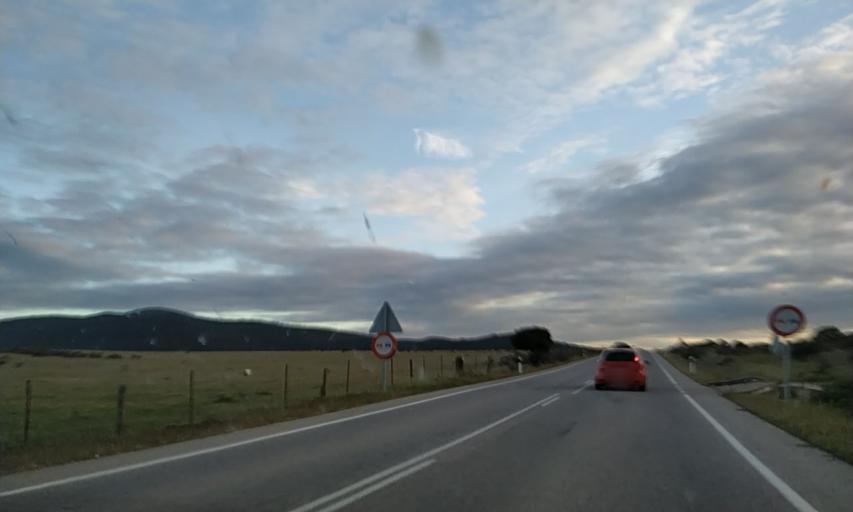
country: ES
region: Extremadura
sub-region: Provincia de Caceres
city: Malpartida de Caceres
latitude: 39.3242
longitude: -6.4968
